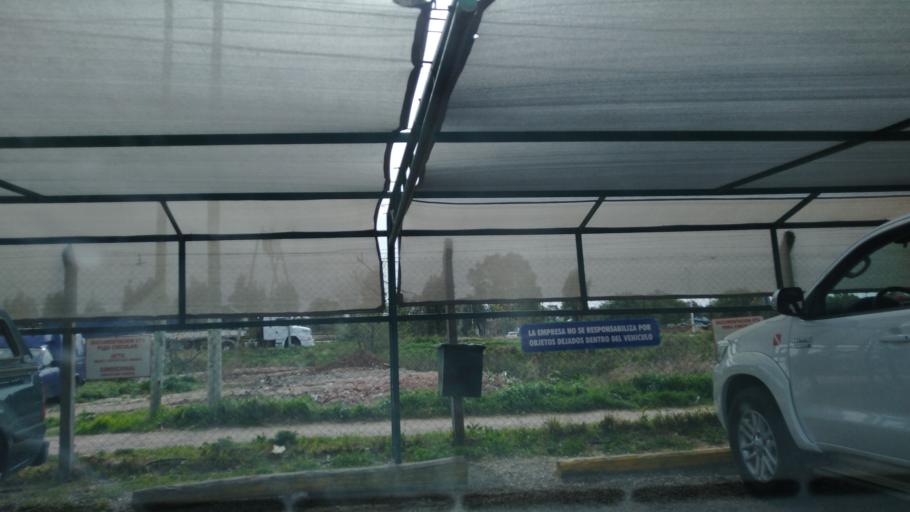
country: AR
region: Buenos Aires
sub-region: Partido de Bahia Blanca
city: Bahia Blanca
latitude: -38.7005
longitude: -62.3300
